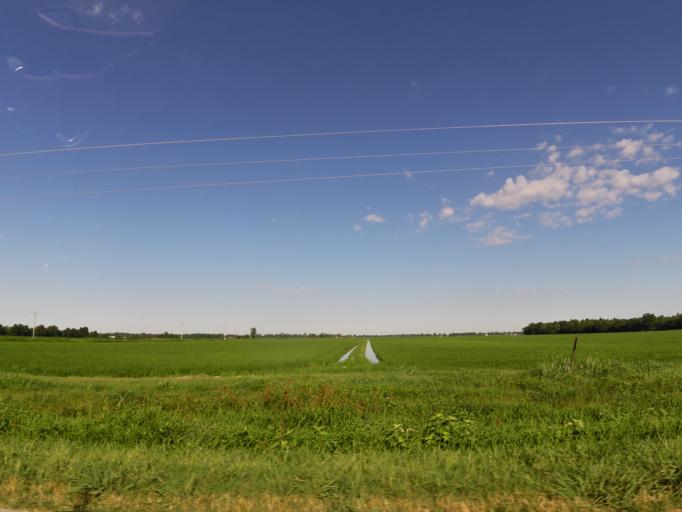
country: US
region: Arkansas
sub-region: Clay County
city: Corning
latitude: 36.5186
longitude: -90.5397
